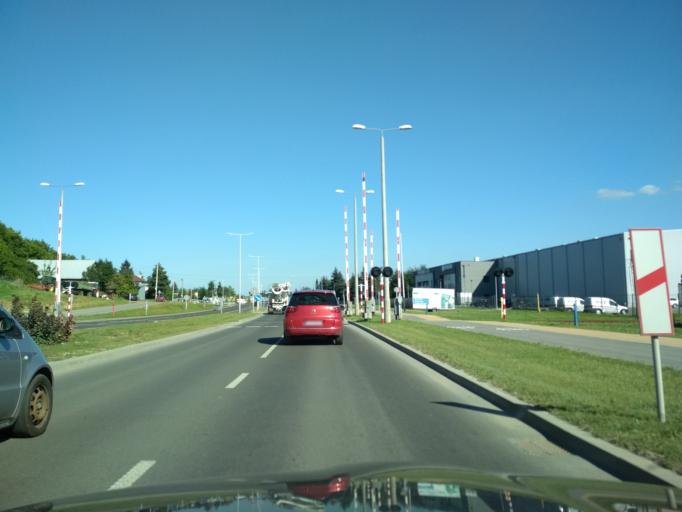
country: PL
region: Subcarpathian Voivodeship
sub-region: Powiat rzeszowski
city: Trzebownisko
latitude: 50.0562
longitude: 22.0288
